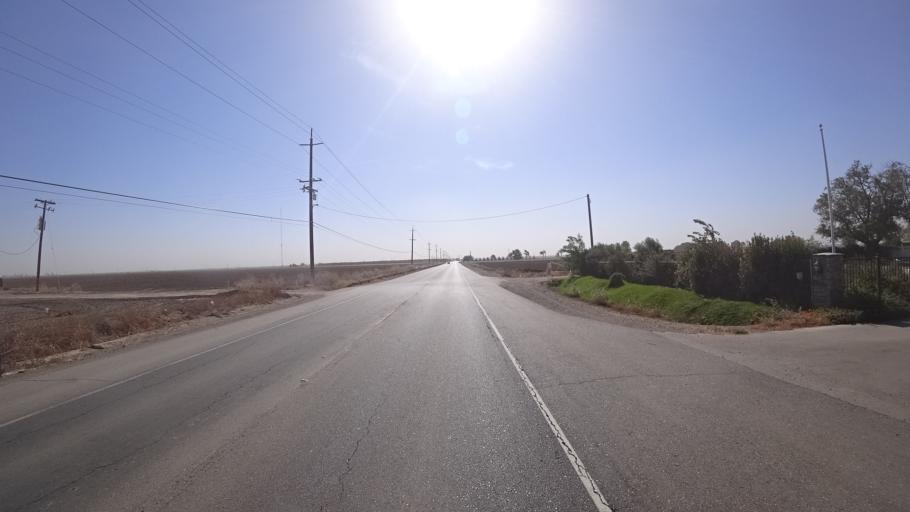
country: US
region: California
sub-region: Yolo County
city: Davis
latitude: 38.5974
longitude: -121.7301
